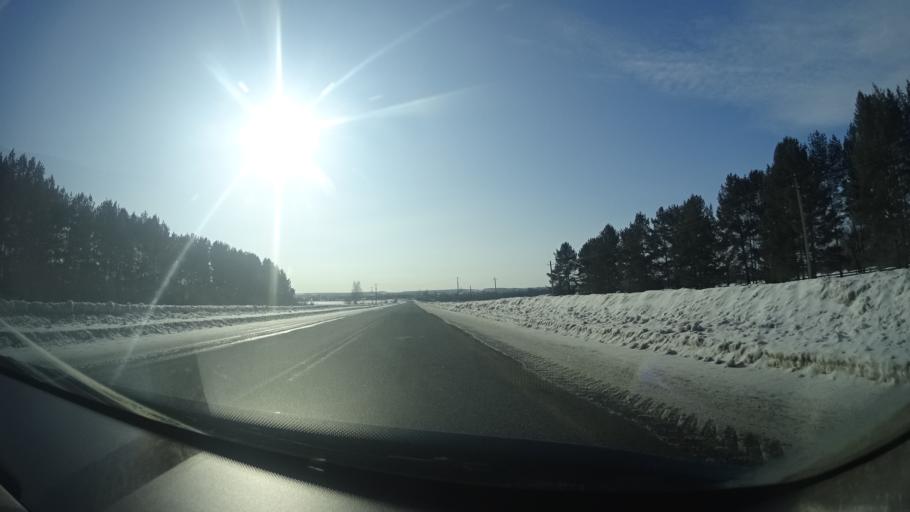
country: RU
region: Perm
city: Kuyeda
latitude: 56.4652
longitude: 55.5923
